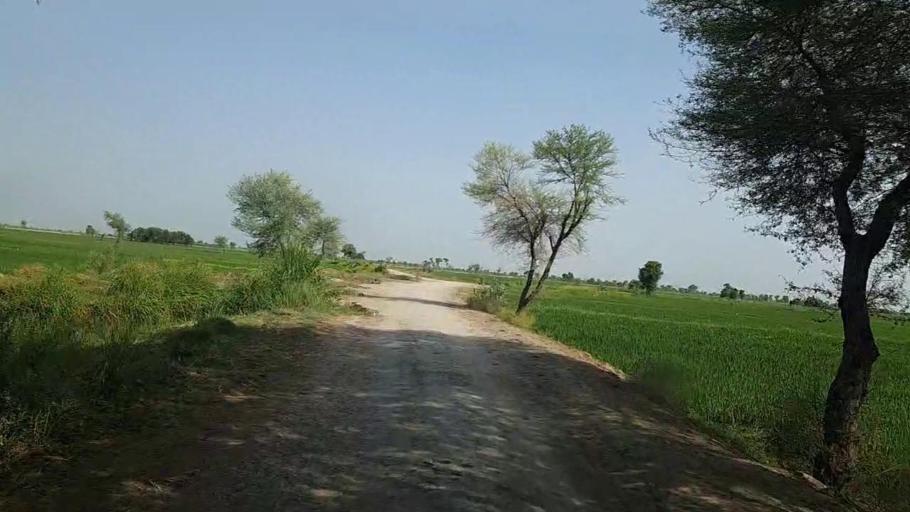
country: PK
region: Sindh
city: Sita Road
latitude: 27.1070
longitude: 67.8500
